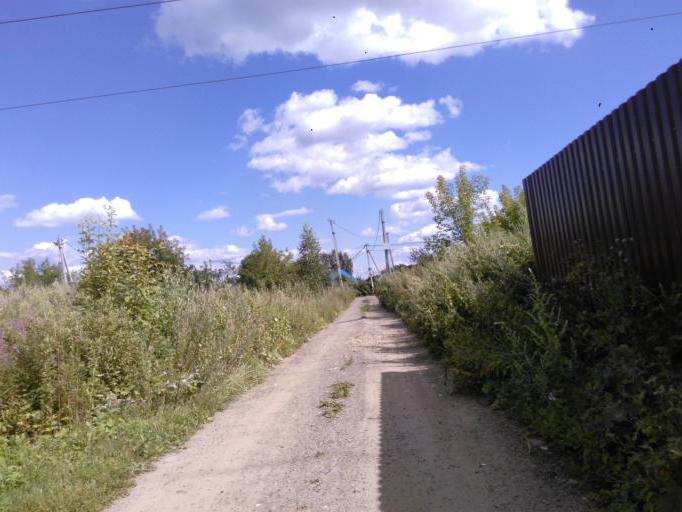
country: RU
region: Moskovskaya
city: Solnechnogorsk
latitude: 56.1338
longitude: 36.9135
